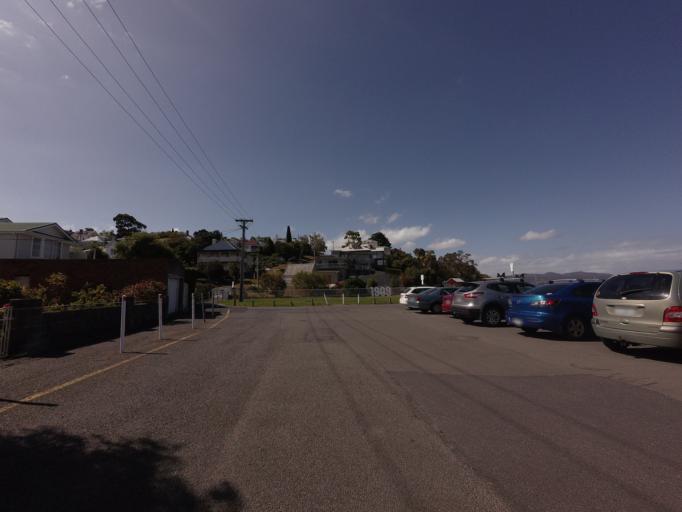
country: AU
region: Tasmania
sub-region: Hobart
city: Sandy Bay
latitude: -42.8947
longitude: 147.3333
